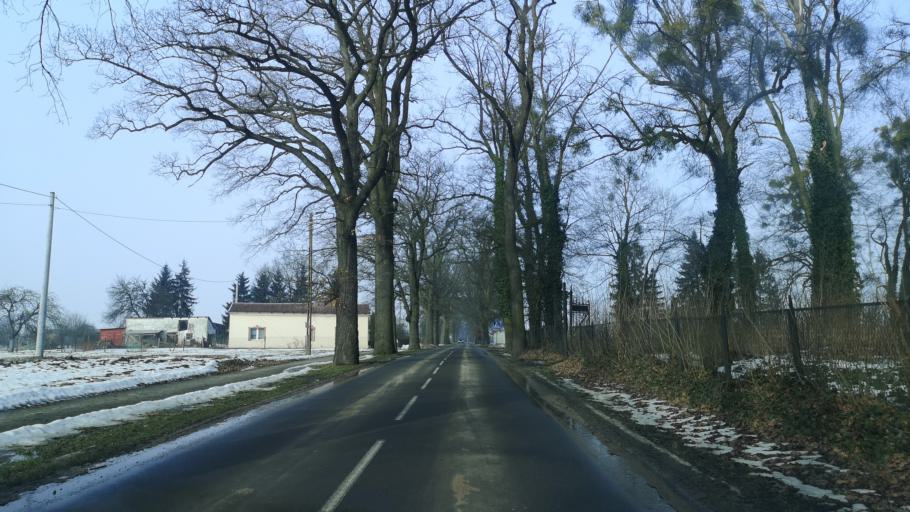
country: PL
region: Warmian-Masurian Voivodeship
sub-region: Powiat nowomiejski
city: Biskupiec
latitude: 53.5039
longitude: 19.3512
